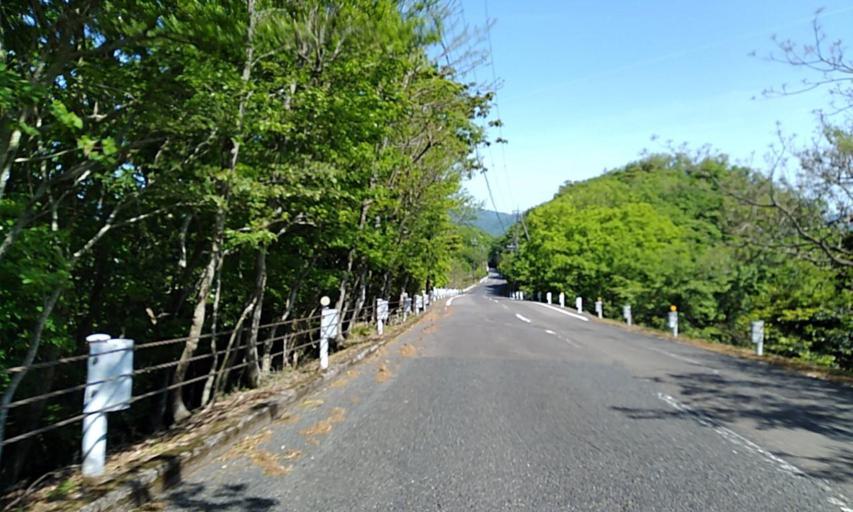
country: JP
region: Fukui
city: Obama
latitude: 35.5442
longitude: 135.7475
